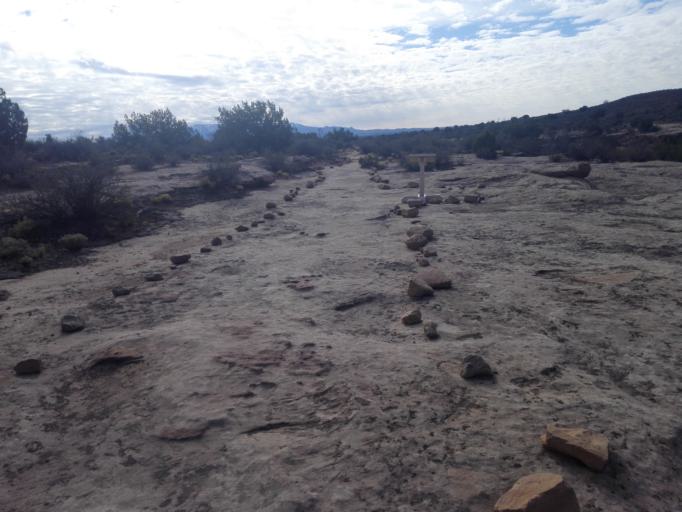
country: US
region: Colorado
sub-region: Montezuma County
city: Towaoc
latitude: 37.3858
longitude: -109.0803
